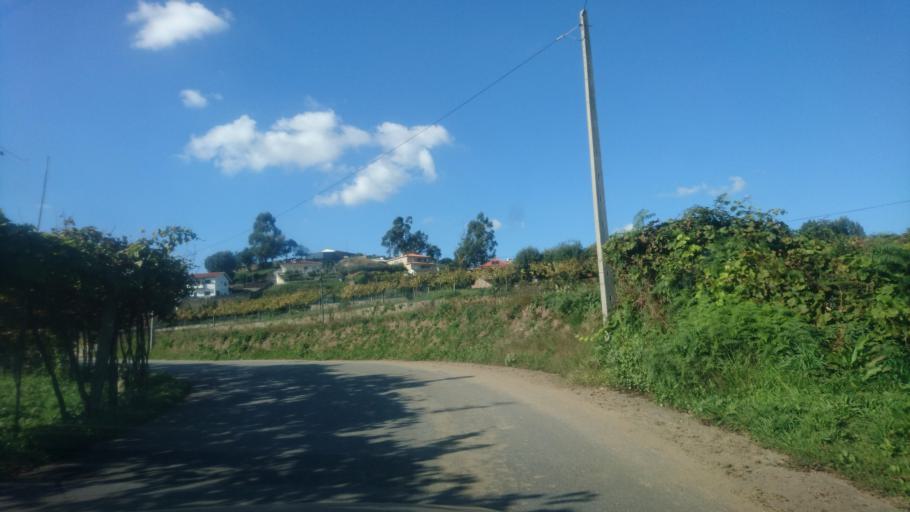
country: PT
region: Porto
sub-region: Paredes
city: Madalena
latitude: 41.2264
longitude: -8.3412
